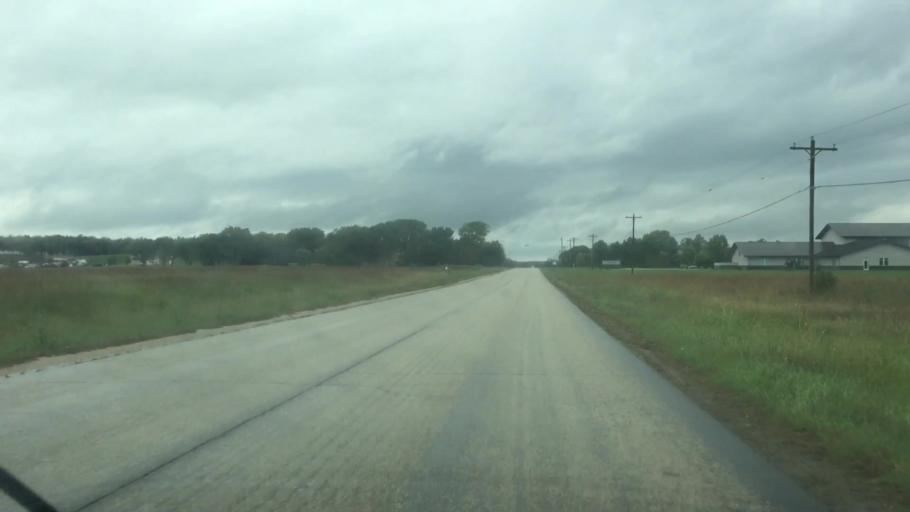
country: US
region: Kansas
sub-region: Allen County
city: Iola
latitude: 37.9513
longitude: -95.3870
